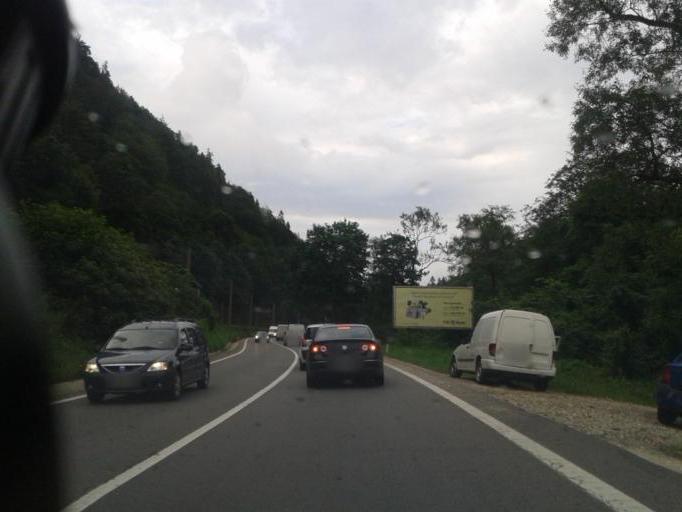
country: RO
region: Brasov
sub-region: Oras Predeal
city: Predeal
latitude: 45.5636
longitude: 25.6033
